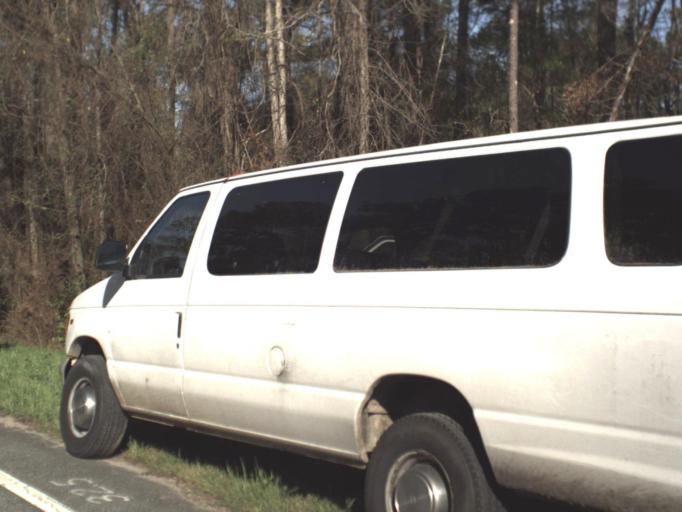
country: US
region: Georgia
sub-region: Seminole County
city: Donalsonville
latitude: 30.9767
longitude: -85.0100
